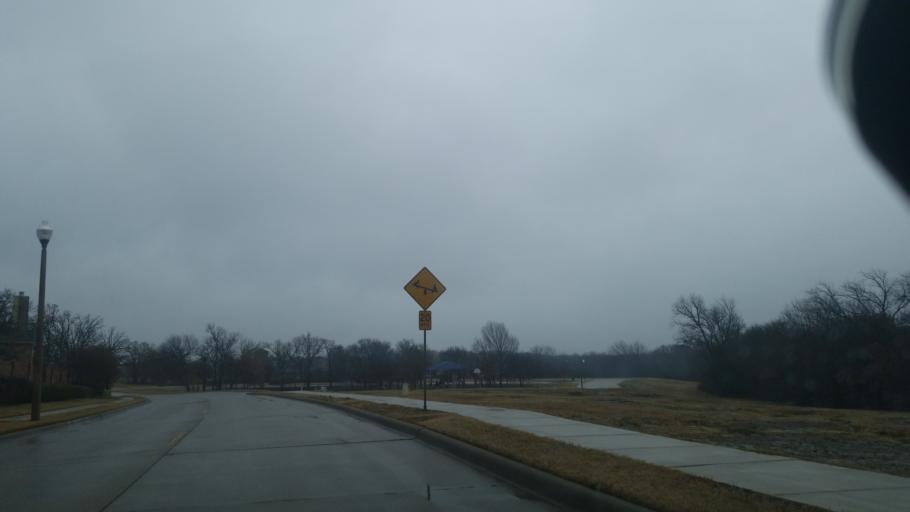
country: US
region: Texas
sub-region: Denton County
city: Corinth
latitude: 33.1749
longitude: -97.0597
